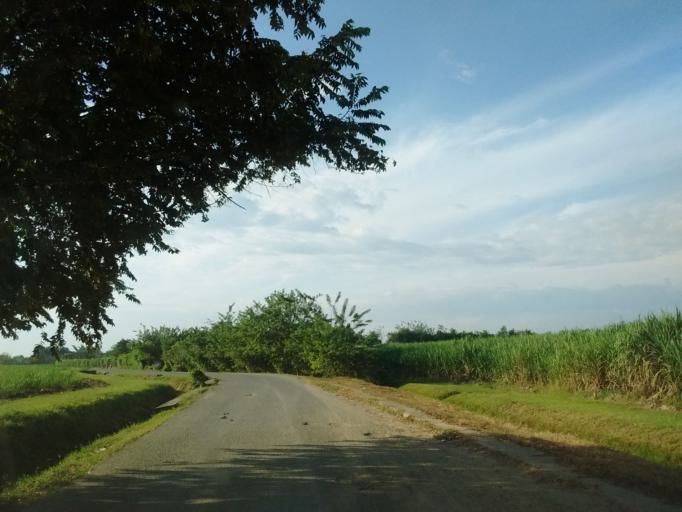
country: CO
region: Cauca
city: Puerto Tejada
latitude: 3.2104
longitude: -76.4438
